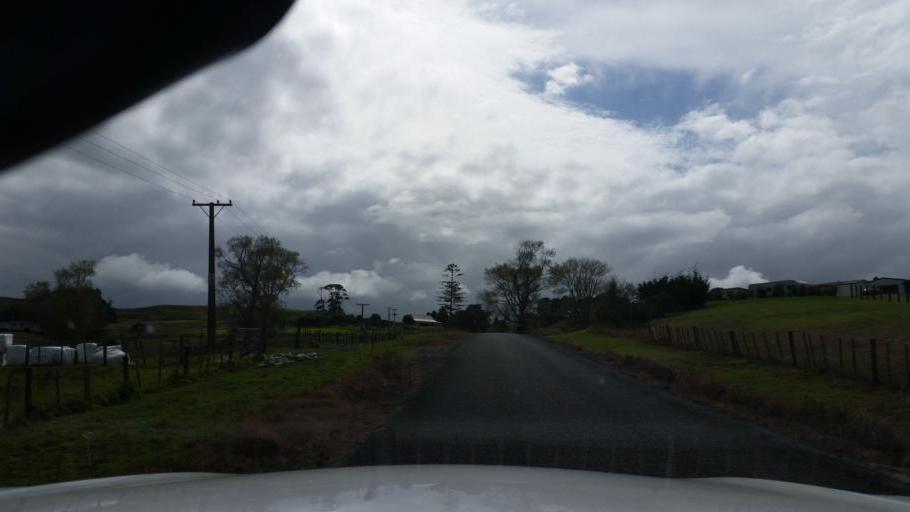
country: NZ
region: Northland
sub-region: Whangarei
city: Ruakaka
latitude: -36.1086
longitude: 174.2773
